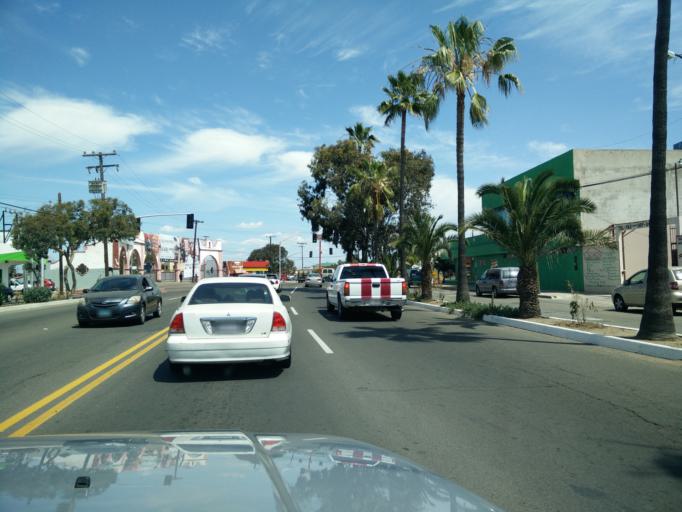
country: US
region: California
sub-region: San Diego County
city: Imperial Beach
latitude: 32.5304
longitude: -117.1199
